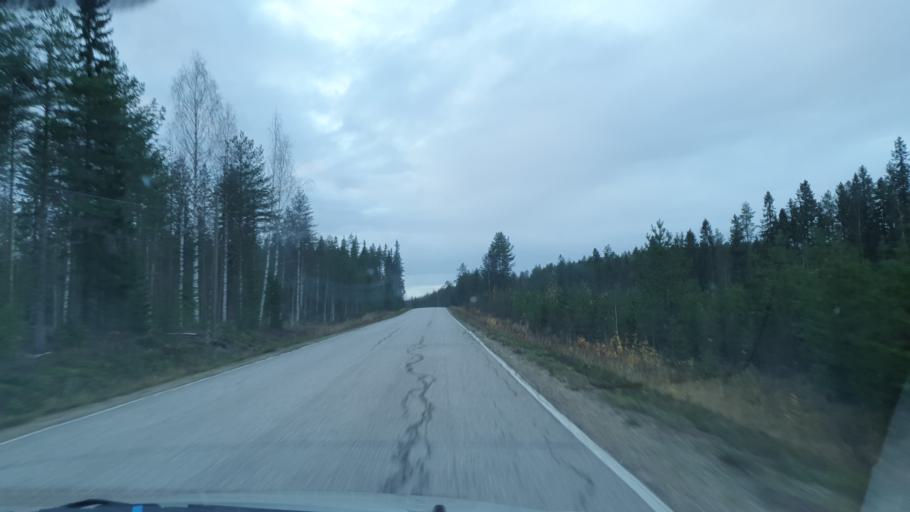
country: FI
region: Kainuu
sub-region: Kajaani
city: Ristijaervi
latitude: 64.4235
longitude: 28.3999
